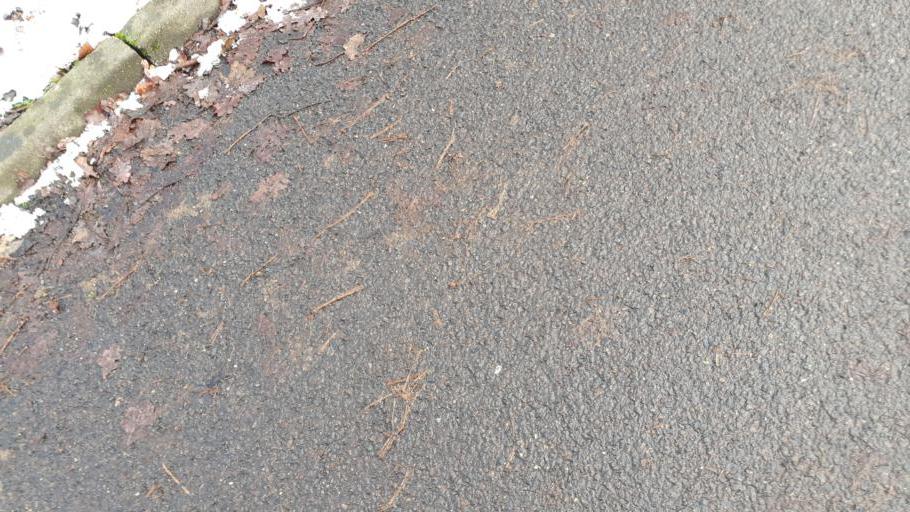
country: DE
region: Saxony
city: Taucha
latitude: 51.3947
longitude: 12.4836
